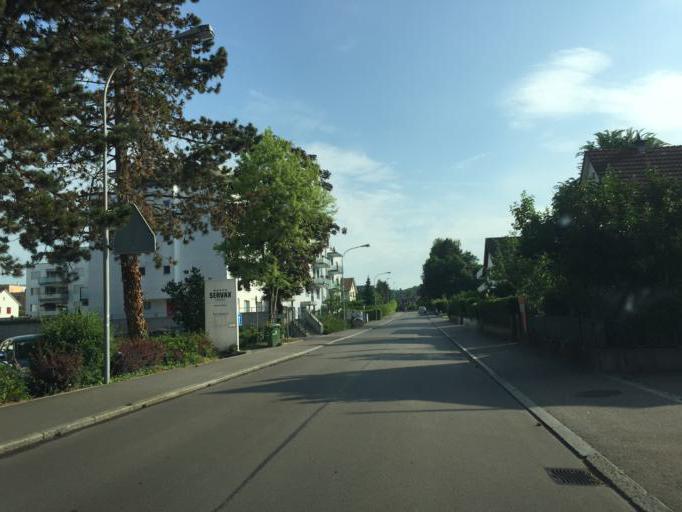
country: CH
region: Zurich
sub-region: Bezirk Buelach
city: Bulach
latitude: 47.5228
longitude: 8.5425
